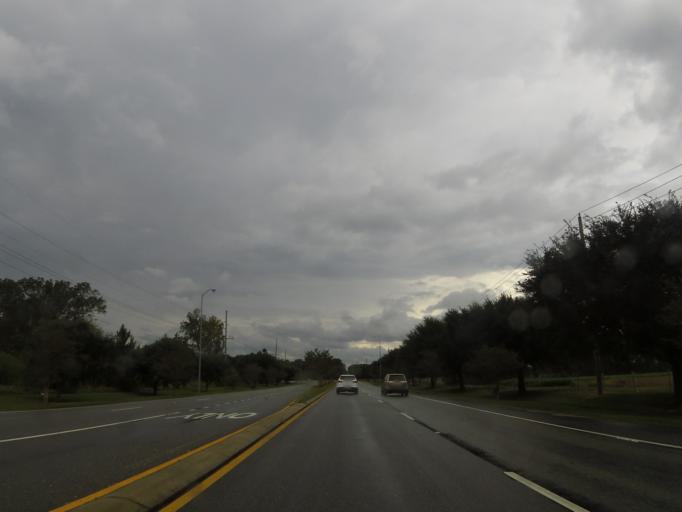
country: US
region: Alabama
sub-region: Baldwin County
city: Fairhope
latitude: 30.5350
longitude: -87.8861
